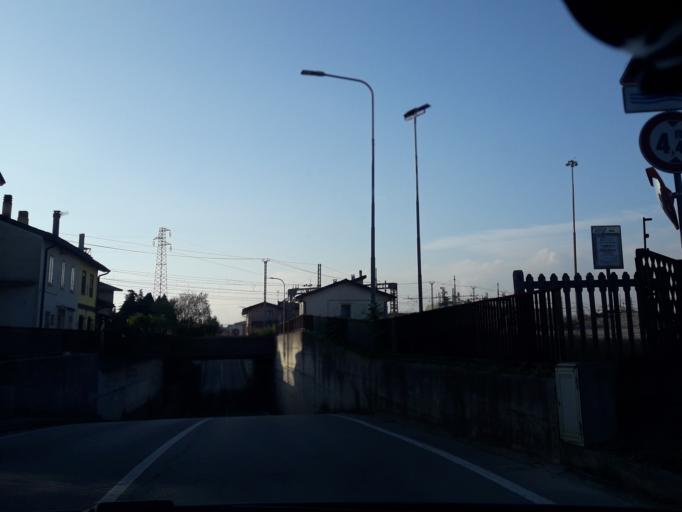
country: IT
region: Friuli Venezia Giulia
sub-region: Provincia di Udine
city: Udine
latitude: 46.0519
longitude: 13.2618
